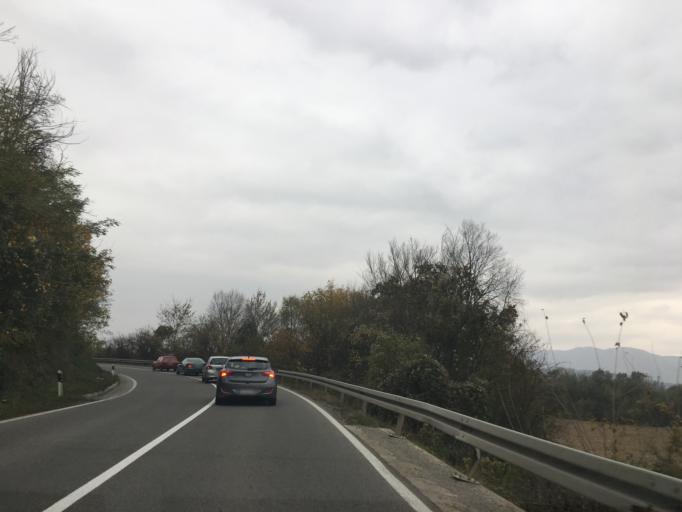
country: RS
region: Central Serbia
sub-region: Raski Okrug
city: Kraljevo
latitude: 43.7136
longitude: 20.7847
